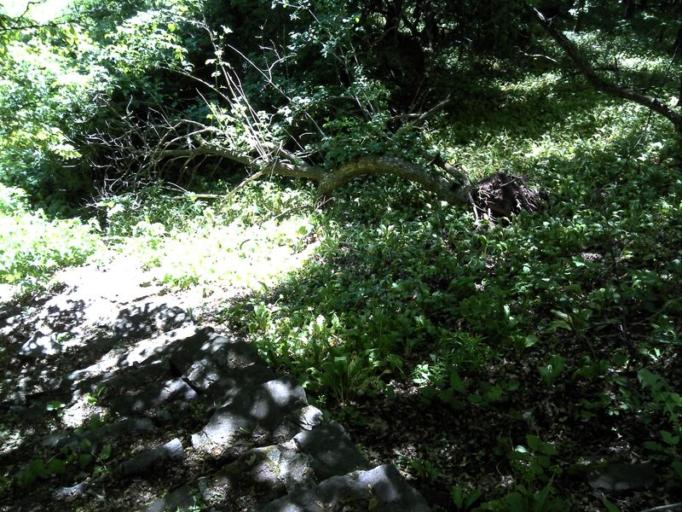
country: HU
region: Baranya
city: Pellerd
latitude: 46.0945
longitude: 18.1381
